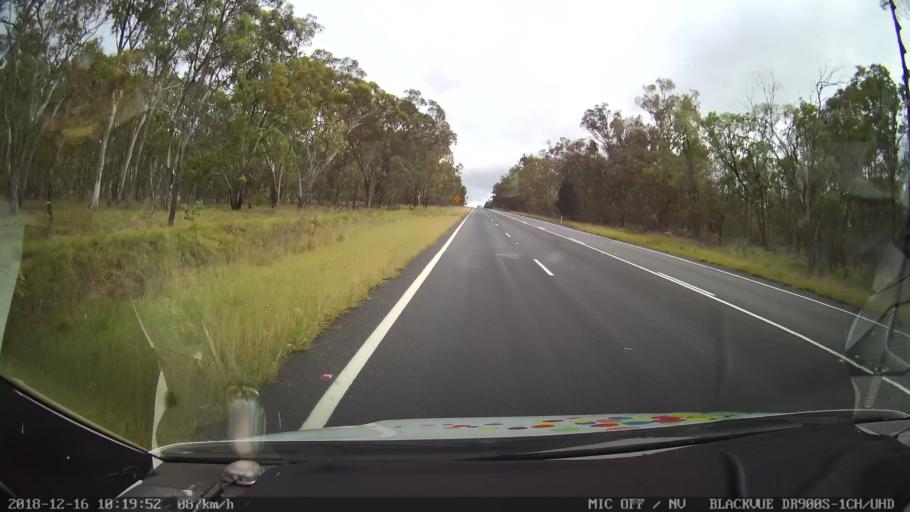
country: AU
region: New South Wales
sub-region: Tenterfield Municipality
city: Carrolls Creek
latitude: -29.2274
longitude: 152.0088
